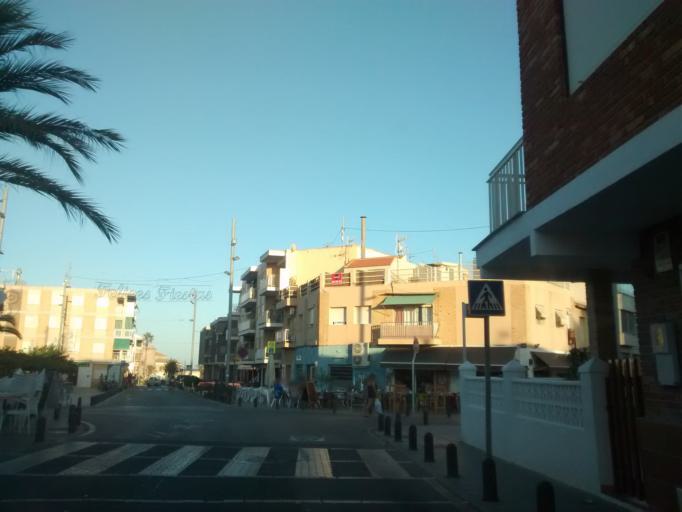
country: ES
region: Valencia
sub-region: Provincia de Alicante
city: Pilar de la Horadada
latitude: 37.8685
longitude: -0.7598
